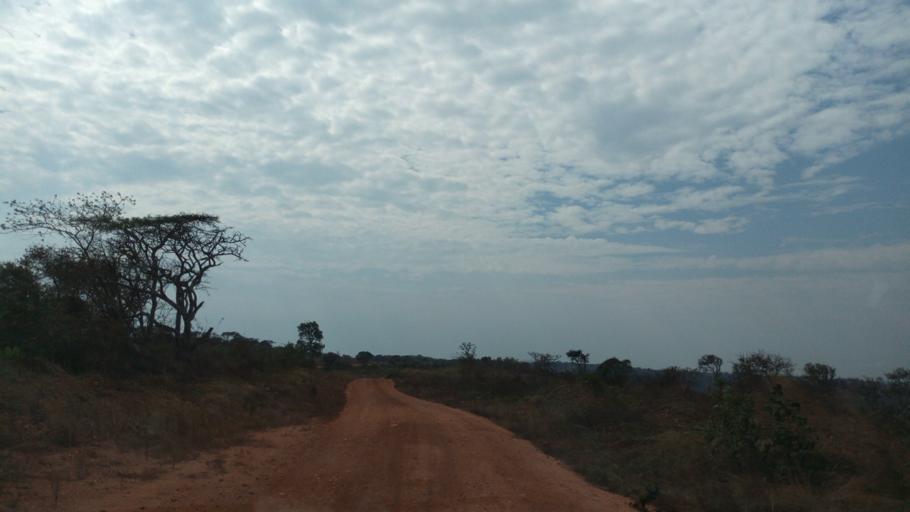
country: CD
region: Katanga
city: Kalemie
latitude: -6.1026
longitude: 28.8893
